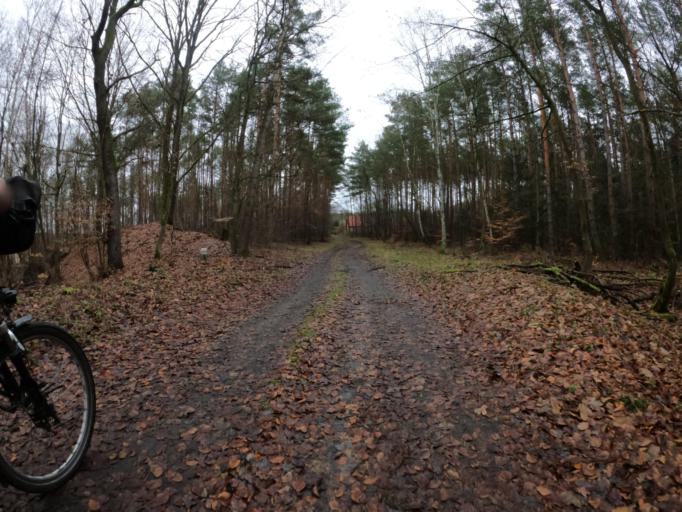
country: PL
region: West Pomeranian Voivodeship
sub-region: Powiat mysliborski
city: Debno
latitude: 52.7399
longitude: 14.7673
